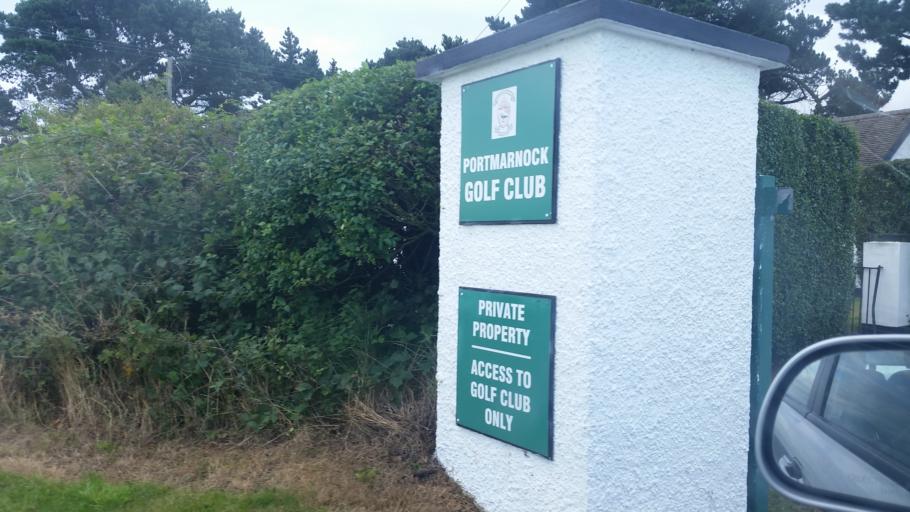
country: IE
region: Leinster
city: Portmarnock
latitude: 53.4154
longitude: -6.1279
